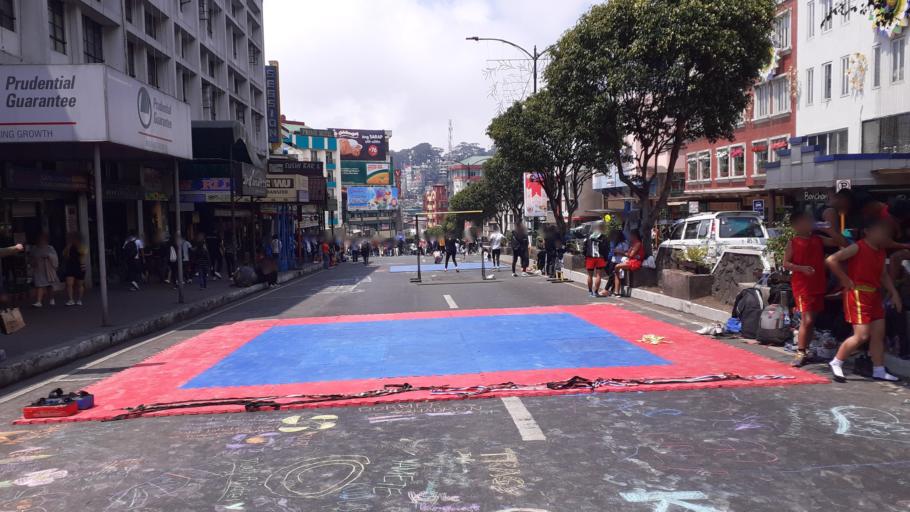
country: PH
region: Cordillera
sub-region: Baguio City
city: Baguio
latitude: 16.4120
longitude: 120.5980
